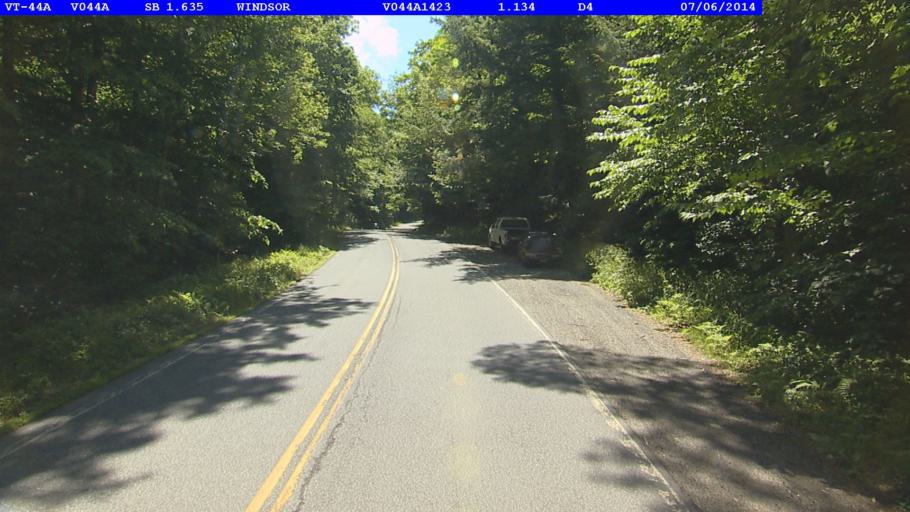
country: US
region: Vermont
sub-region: Windsor County
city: Windsor
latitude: 43.4426
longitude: -72.4119
